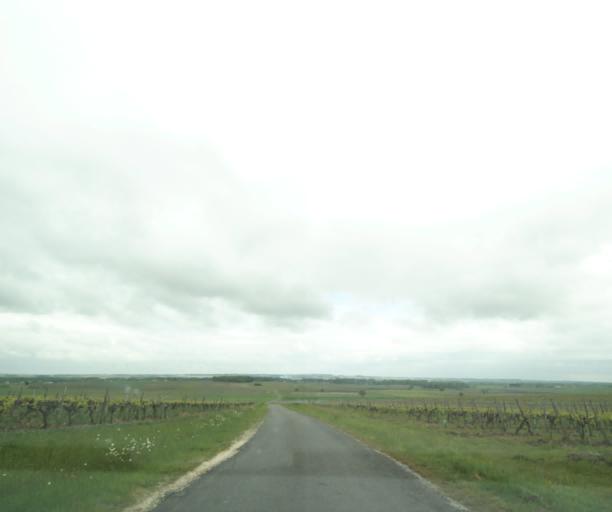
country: FR
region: Poitou-Charentes
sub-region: Departement de la Charente-Maritime
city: Perignac
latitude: 45.6640
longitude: -0.5013
